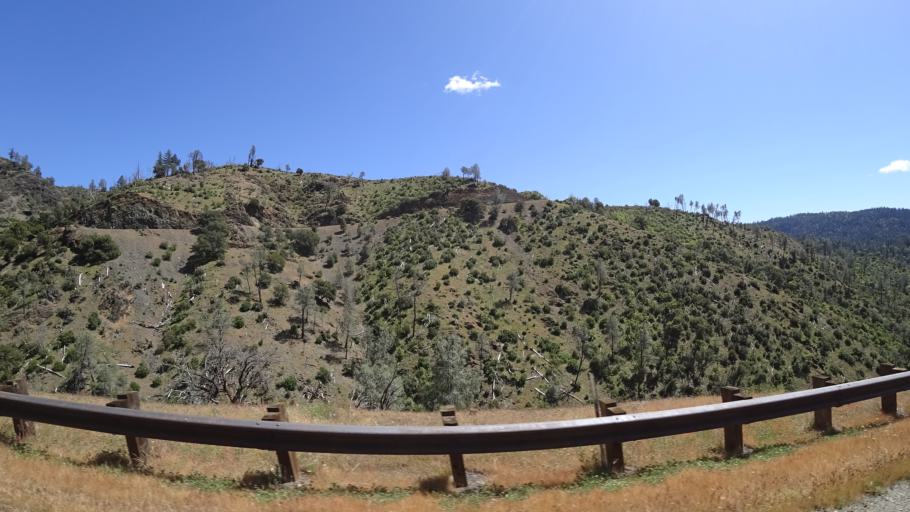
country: US
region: California
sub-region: Trinity County
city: Weaverville
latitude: 40.7413
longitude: -123.0021
